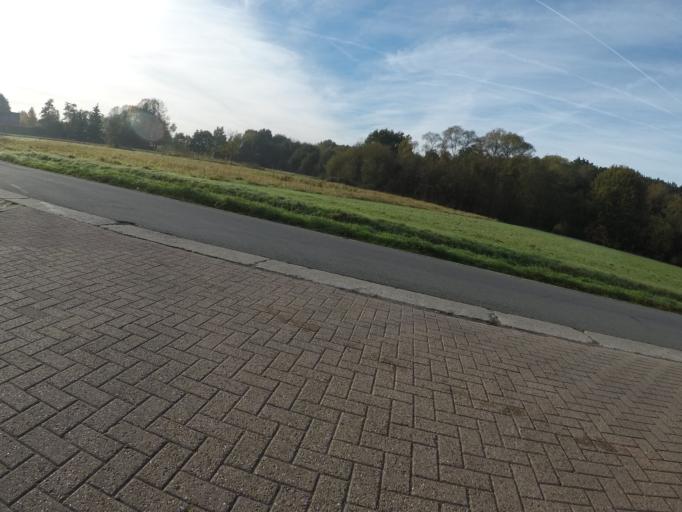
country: BE
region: Flanders
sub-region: Provincie Vlaams-Brabant
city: Begijnendijk
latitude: 50.9959
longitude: 4.7715
